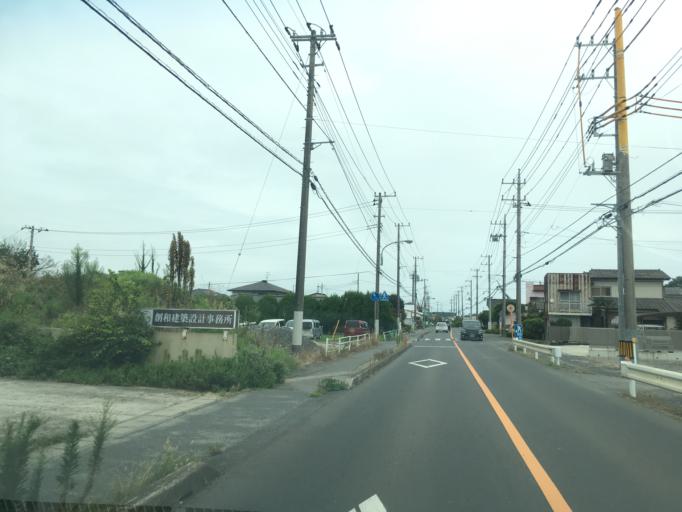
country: JP
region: Ibaraki
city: Hitachi-Naka
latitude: 36.4043
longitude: 140.5569
